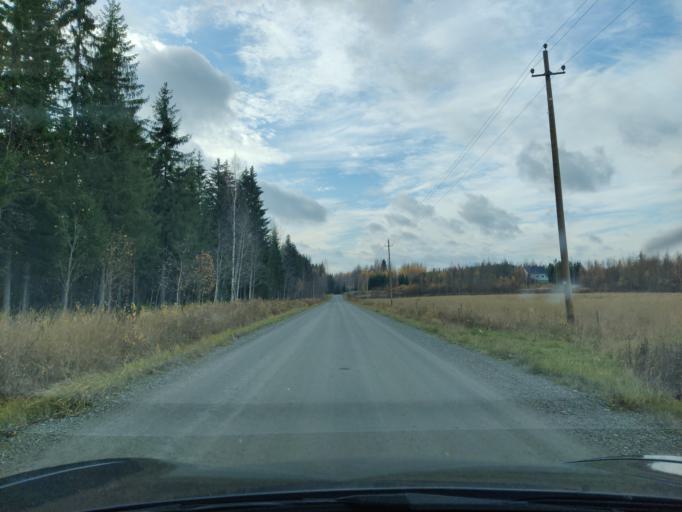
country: FI
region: Northern Savo
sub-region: Kuopio
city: Siilinjaervi
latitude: 63.1210
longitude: 27.5485
